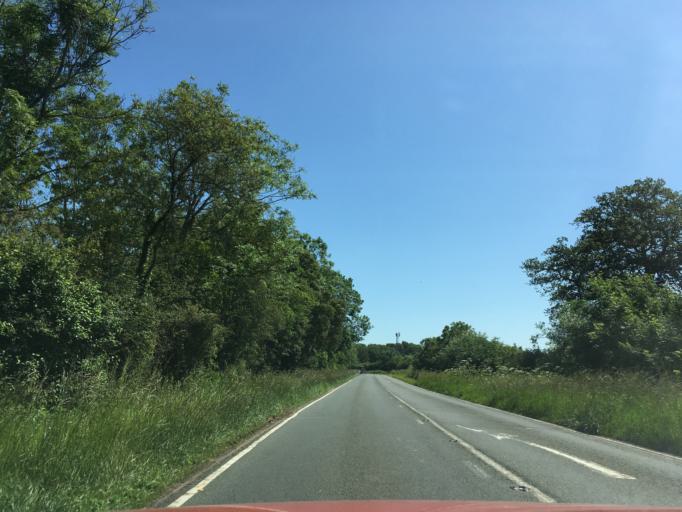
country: GB
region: England
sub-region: Oxfordshire
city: Hook Norton
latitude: 51.9714
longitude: -1.4614
